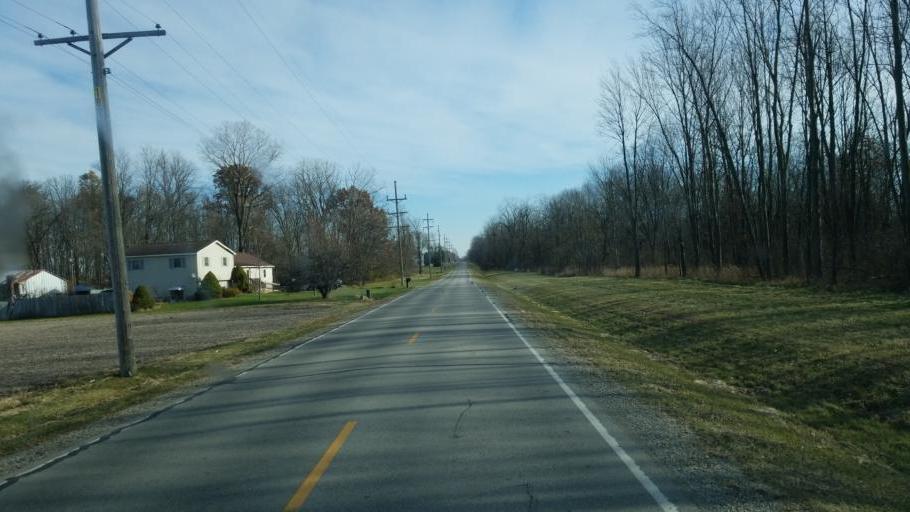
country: US
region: Ohio
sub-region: Crawford County
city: Crestline
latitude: 40.7850
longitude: -82.7771
